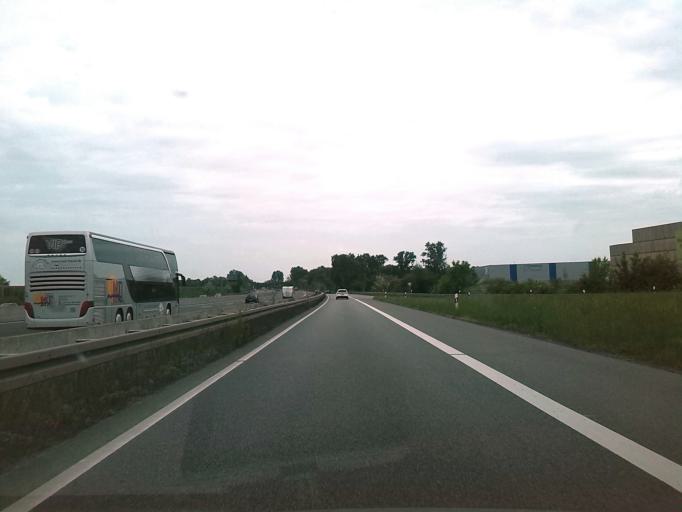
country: DE
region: Hesse
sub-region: Regierungsbezirk Darmstadt
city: Einhausen
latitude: 49.6630
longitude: 8.5551
